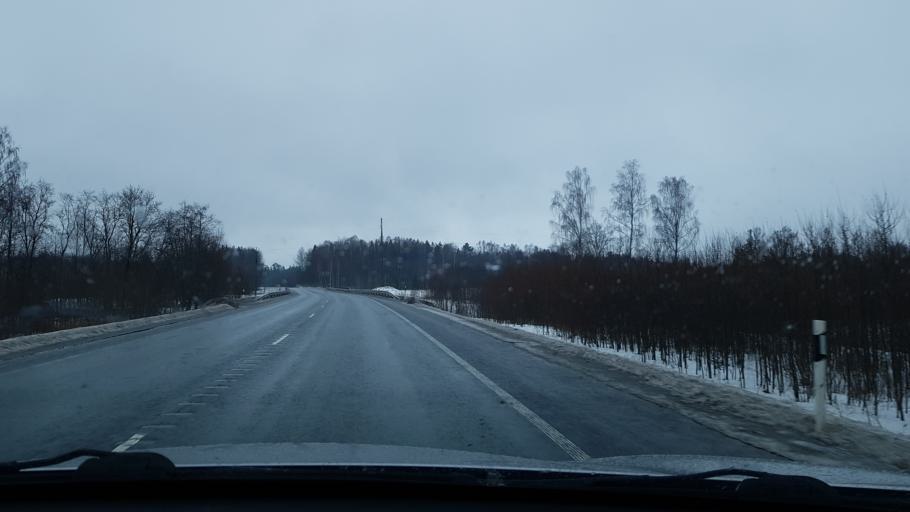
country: EE
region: Raplamaa
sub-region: Kohila vald
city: Kohila
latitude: 59.1363
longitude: 24.7920
